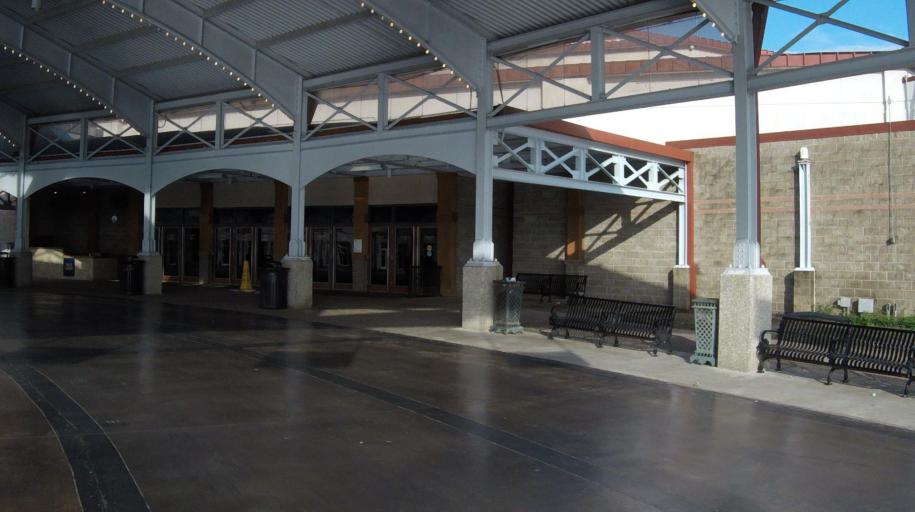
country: US
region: Louisiana
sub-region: Allen Parish
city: Kinder
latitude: 30.5458
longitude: -92.8138
